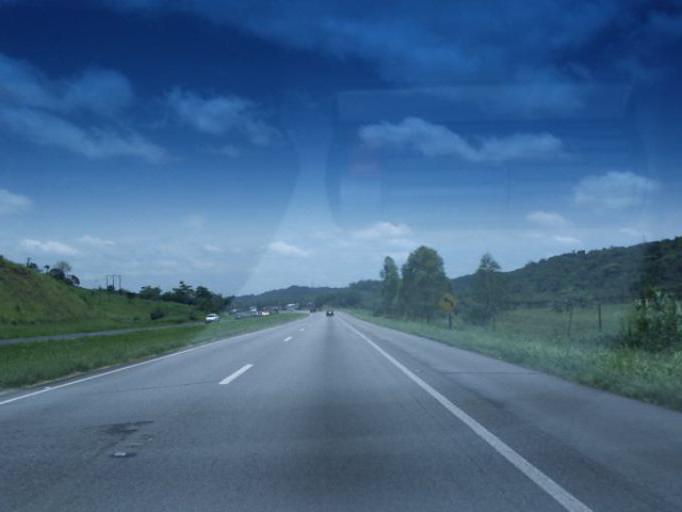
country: BR
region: Sao Paulo
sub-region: Registro
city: Registro
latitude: -24.4216
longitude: -47.7749
